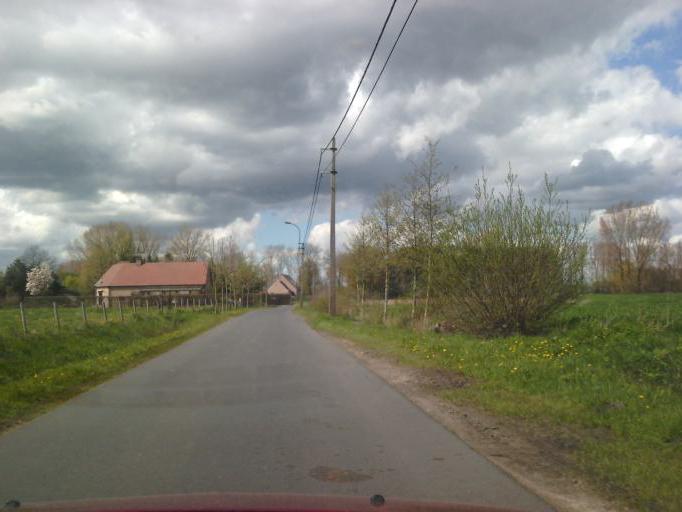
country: BE
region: Flanders
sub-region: Provincie Oost-Vlaanderen
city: Lokeren
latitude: 51.0783
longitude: 3.9198
